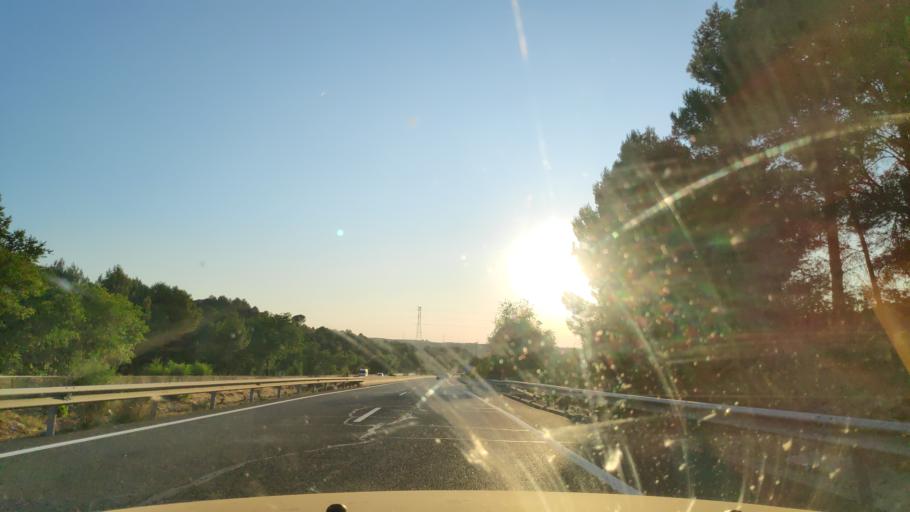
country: ES
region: Madrid
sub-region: Provincia de Madrid
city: Arganda
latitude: 40.2688
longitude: -3.4302
